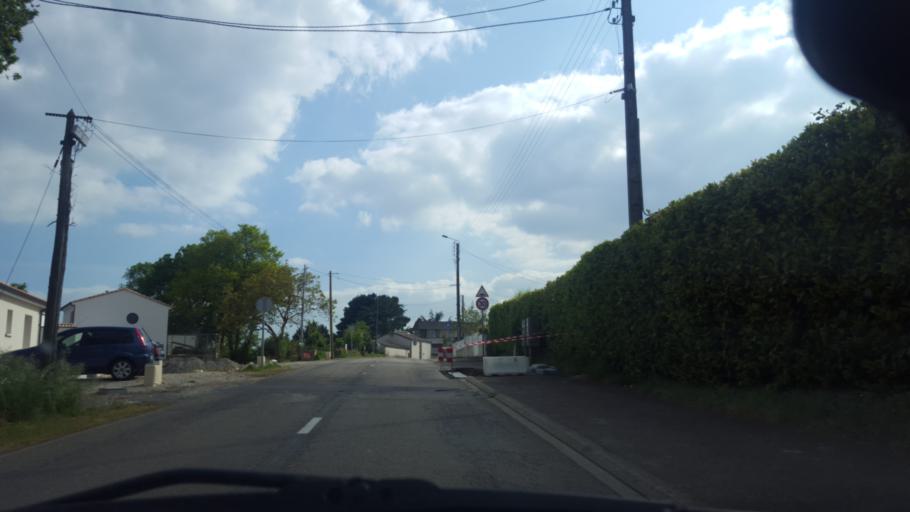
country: FR
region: Pays de la Loire
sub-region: Departement de la Loire-Atlantique
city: La Limouziniere
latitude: 46.9952
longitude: -1.5936
